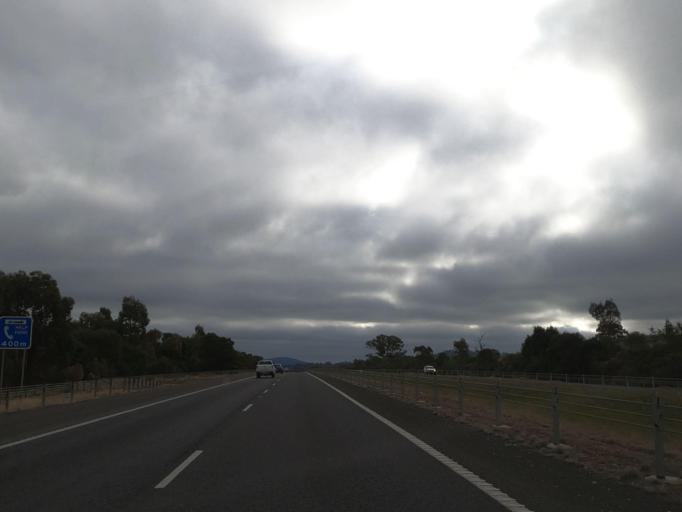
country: AU
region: Victoria
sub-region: Mount Alexander
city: Castlemaine
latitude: -37.0579
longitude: 144.3018
